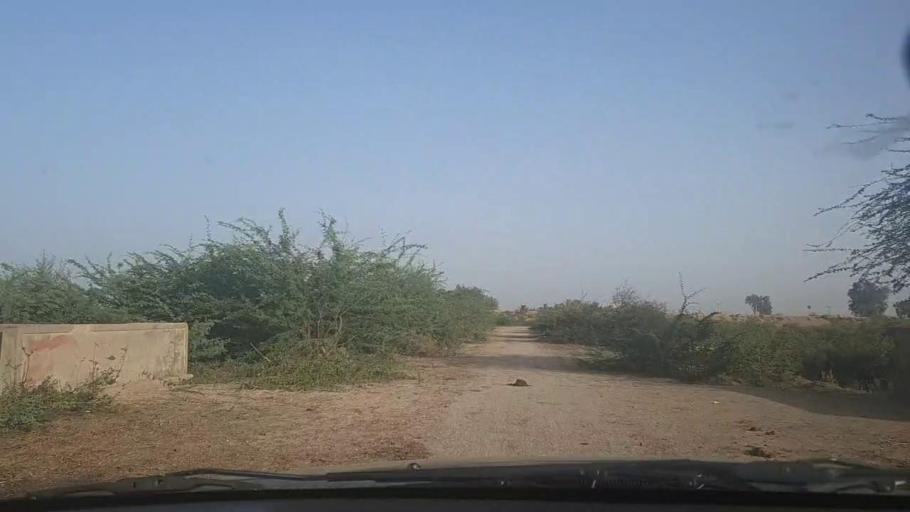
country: PK
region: Sindh
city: Keti Bandar
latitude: 24.2907
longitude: 67.6147
